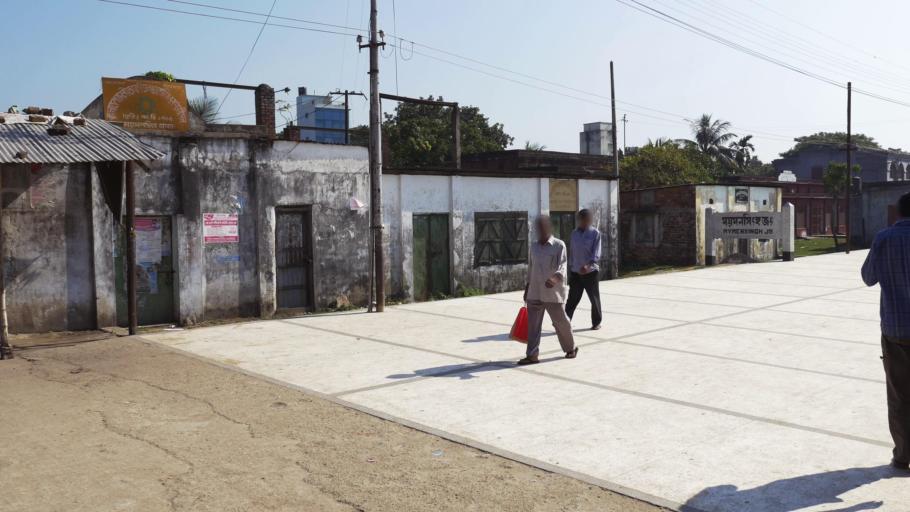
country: BD
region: Dhaka
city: Mymensingh
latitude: 24.6479
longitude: 90.4540
